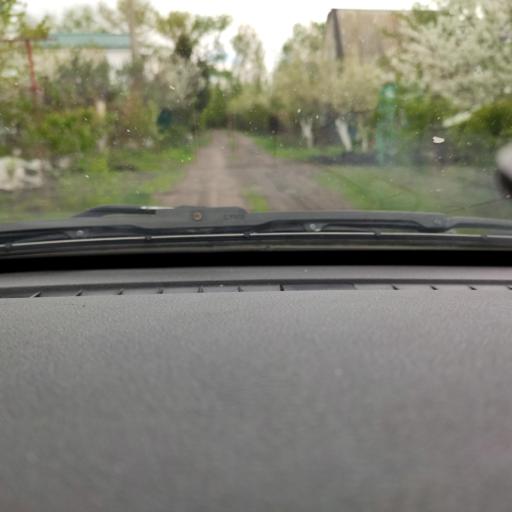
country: RU
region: Voronezj
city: Maslovka
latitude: 51.4950
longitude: 39.2100
